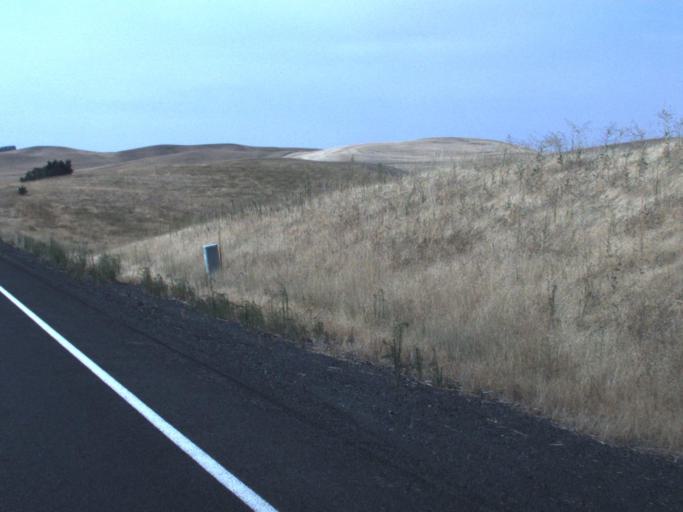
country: US
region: Washington
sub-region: Whitman County
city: Pullman
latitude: 46.7753
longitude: -117.1578
